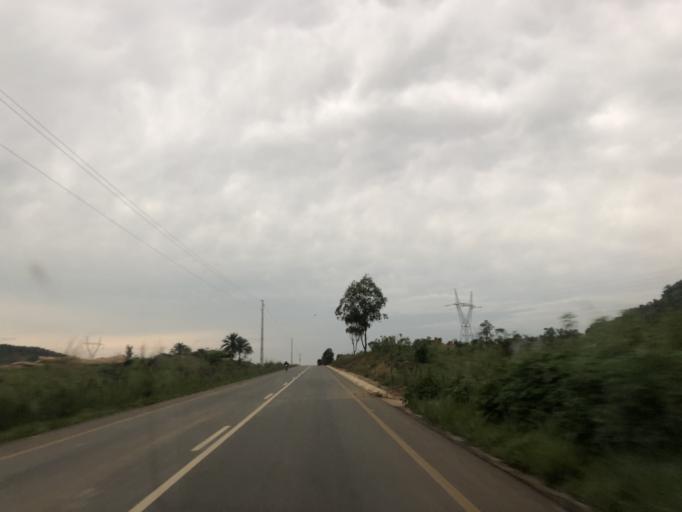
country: AO
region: Cuanza Sul
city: Uacu Cungo
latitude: -11.3215
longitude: 15.0874
